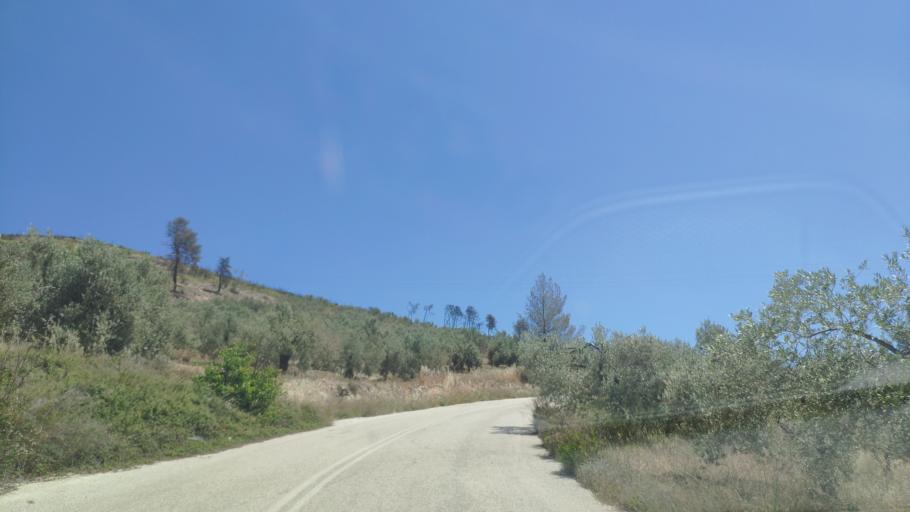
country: GR
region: Peloponnese
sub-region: Nomos Korinthias
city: Athikia
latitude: 37.8365
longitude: 22.9388
